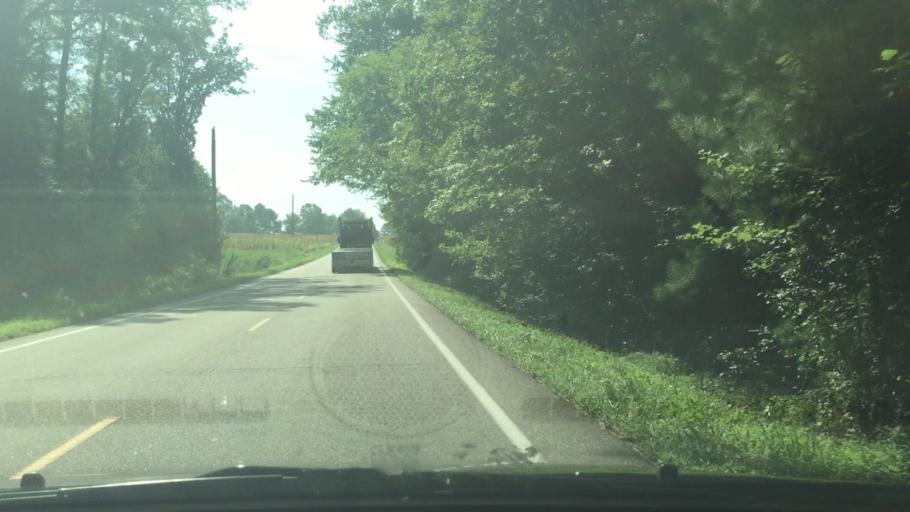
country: US
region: Virginia
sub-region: Prince George County
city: Prince George
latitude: 37.0685
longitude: -77.3388
